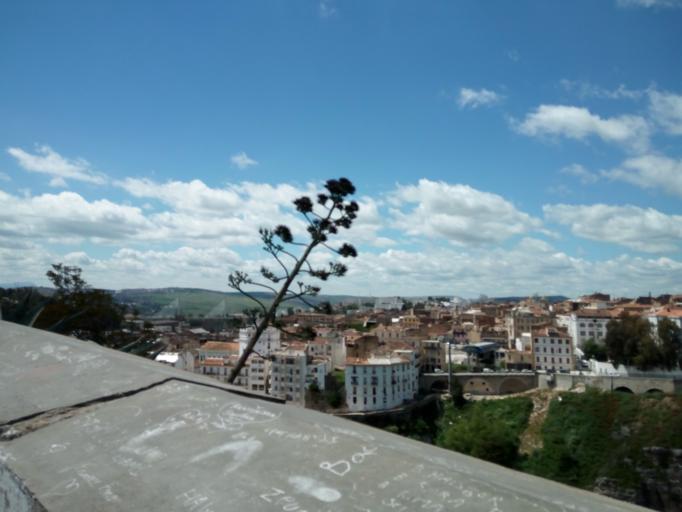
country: DZ
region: Constantine
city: Constantine
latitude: 36.3718
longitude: 6.6166
